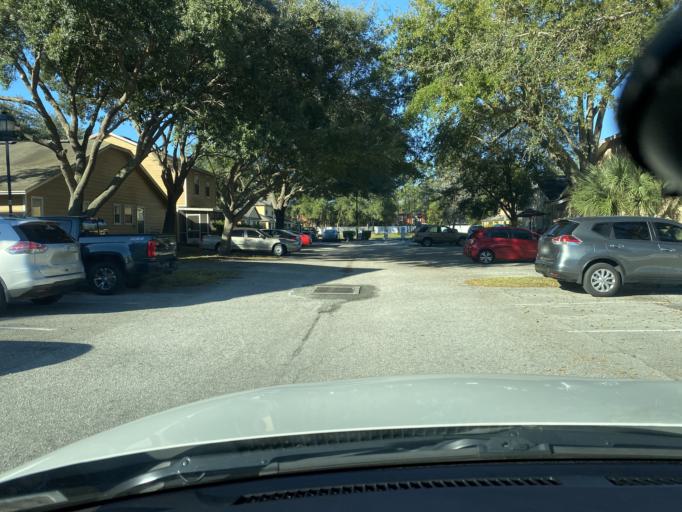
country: US
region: Florida
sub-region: Orange County
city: Conway
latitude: 28.5122
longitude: -81.3048
